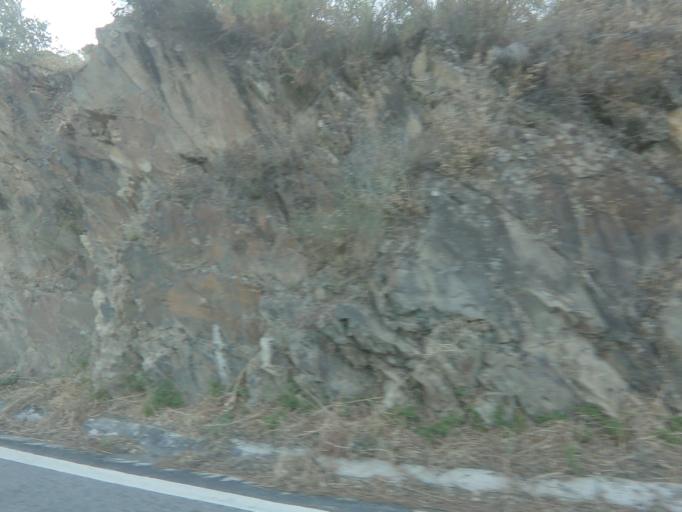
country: PT
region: Viseu
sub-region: Tabuaco
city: Tabuaco
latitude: 41.1244
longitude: -7.5715
